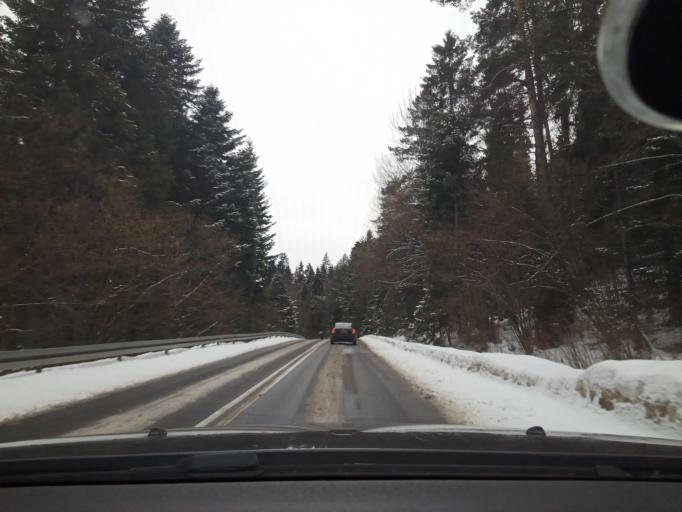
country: PL
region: Lesser Poland Voivodeship
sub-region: Powiat nowotarski
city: Krosnica
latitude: 49.4252
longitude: 20.3497
